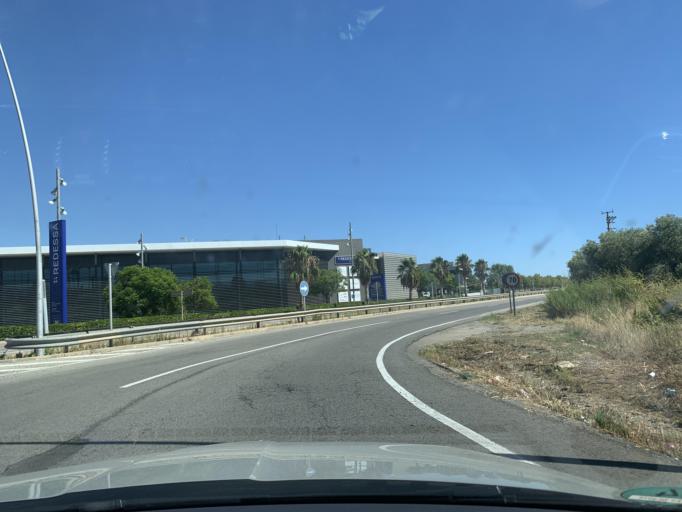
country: ES
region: Catalonia
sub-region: Provincia de Tarragona
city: Reus
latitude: 41.1427
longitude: 1.1278
